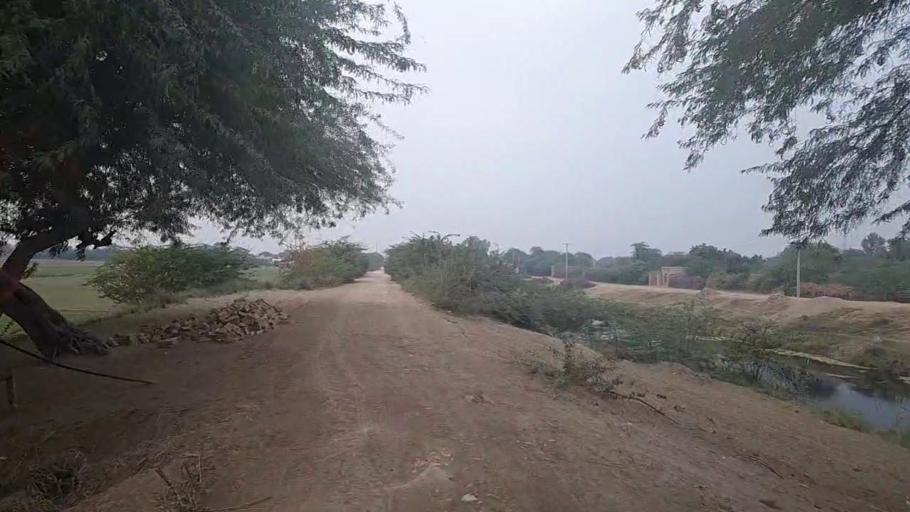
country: PK
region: Sindh
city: Gambat
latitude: 27.3600
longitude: 68.5673
